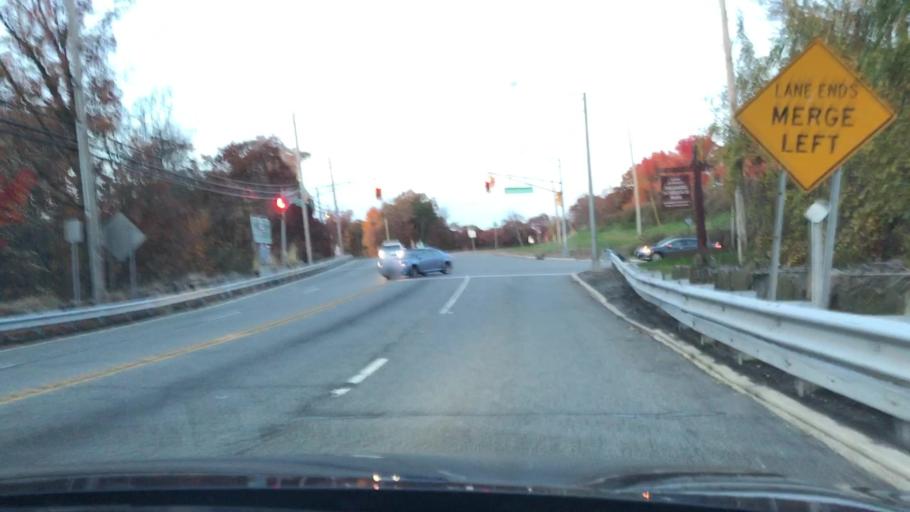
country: US
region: New Jersey
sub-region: Bergen County
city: Alpine
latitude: 40.9561
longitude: -73.9216
